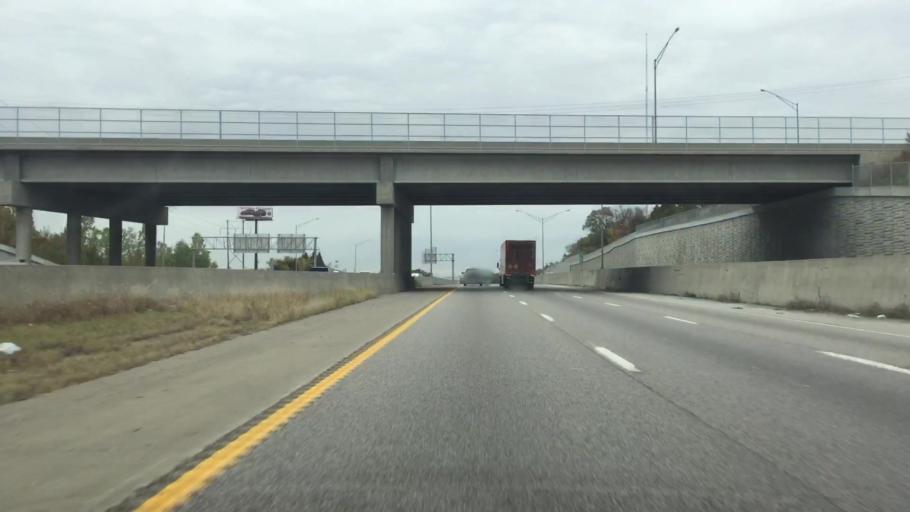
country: US
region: Missouri
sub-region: Jackson County
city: Raytown
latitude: 39.0627
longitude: -94.4882
